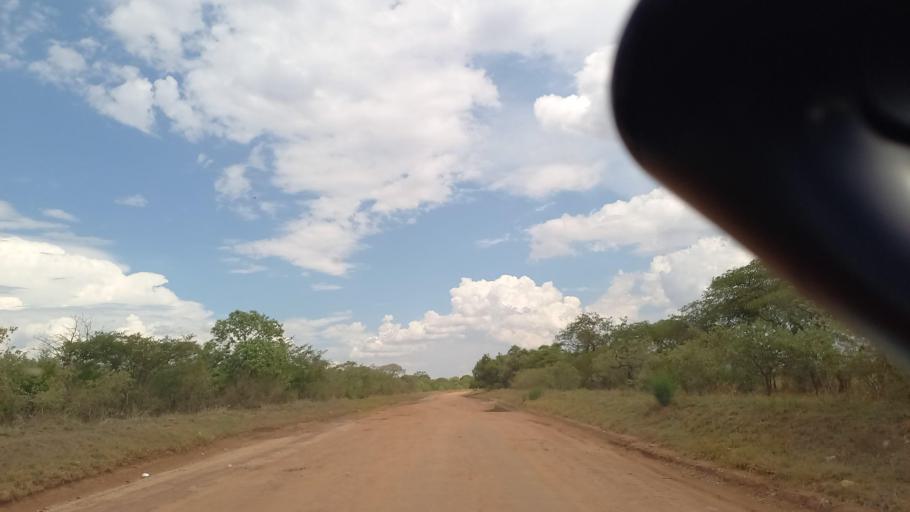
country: ZM
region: Southern
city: Nakambala
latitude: -16.0502
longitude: 27.9827
